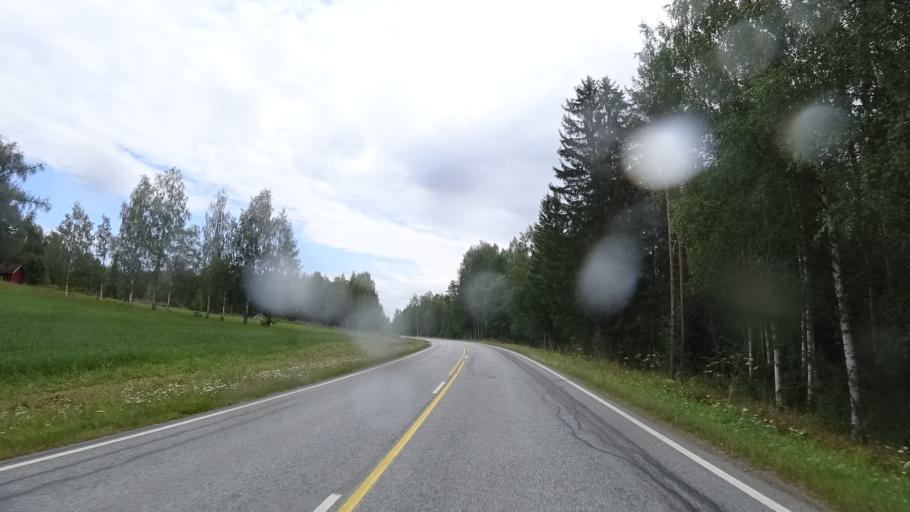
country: FI
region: North Karelia
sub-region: Keski-Karjala
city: Raeaekkylae
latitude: 62.1071
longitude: 29.7026
